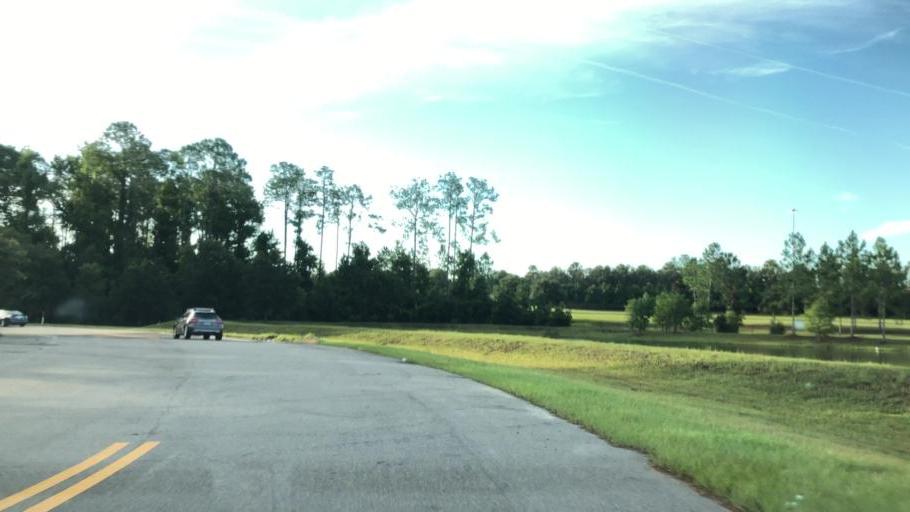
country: US
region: Florida
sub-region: Saint Johns County
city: Palm Valley
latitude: 30.1167
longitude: -81.4161
